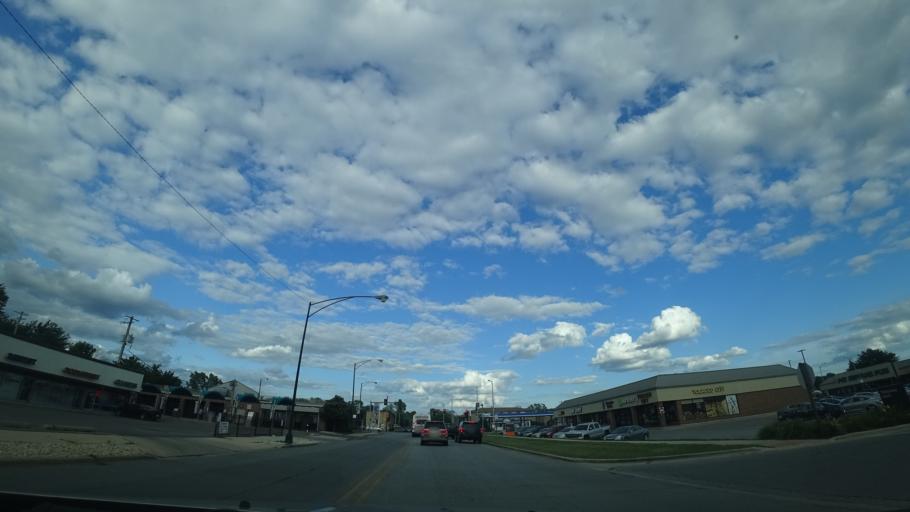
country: US
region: Illinois
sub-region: Cook County
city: Merrionette Park
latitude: 41.6843
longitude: -87.7017
